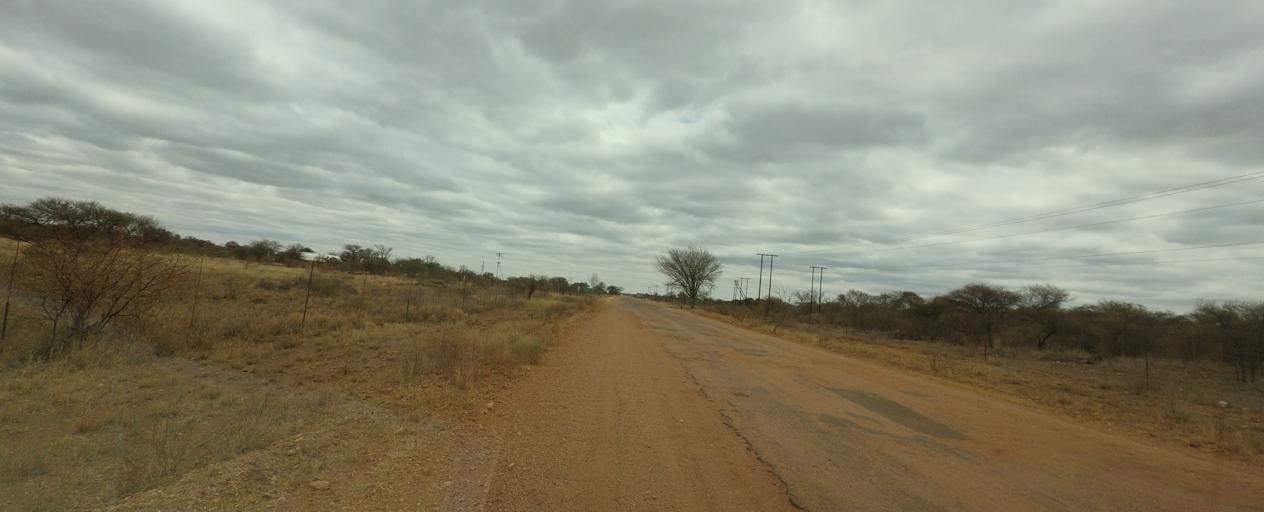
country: BW
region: Central
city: Mathathane
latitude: -22.7439
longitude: 28.4512
